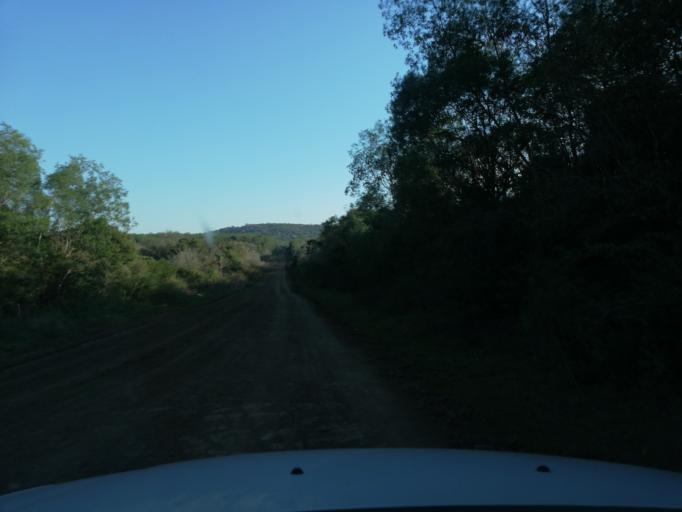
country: AR
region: Misiones
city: Cerro Cora
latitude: -27.5986
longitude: -55.6978
